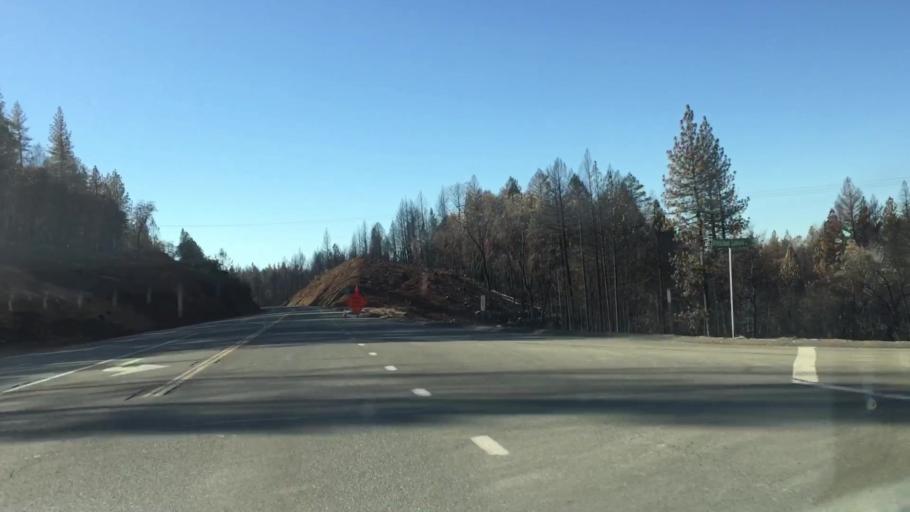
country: US
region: California
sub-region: Butte County
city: Magalia
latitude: 39.7255
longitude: -121.5032
